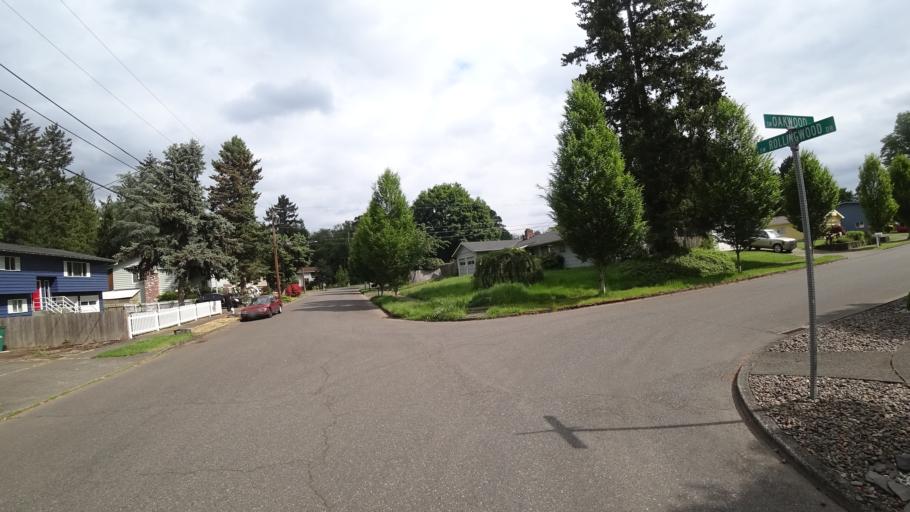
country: US
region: Oregon
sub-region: Washington County
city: Raleigh Hills
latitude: 45.4715
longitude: -122.7801
